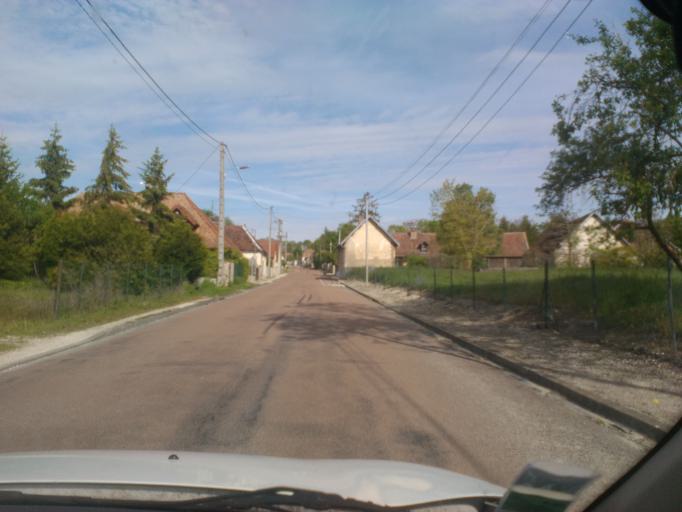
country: FR
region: Champagne-Ardenne
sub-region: Departement de l'Aube
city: Payns
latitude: 48.3699
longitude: 3.8984
